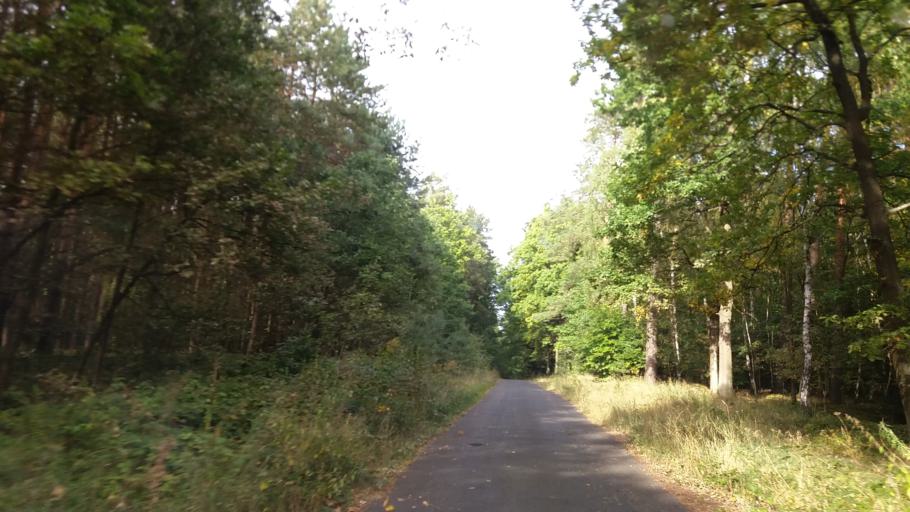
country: PL
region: West Pomeranian Voivodeship
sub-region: Powiat choszczenski
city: Krzecin
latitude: 52.9764
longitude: 15.4599
